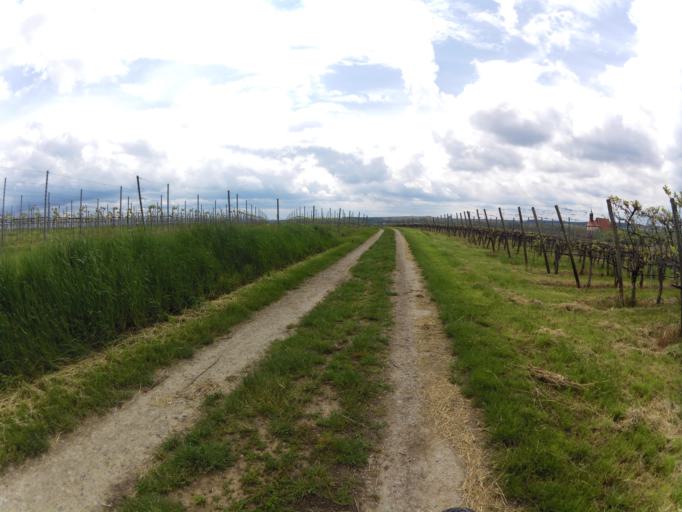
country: DE
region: Bavaria
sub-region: Regierungsbezirk Unterfranken
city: Volkach
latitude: 49.8763
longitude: 10.2178
